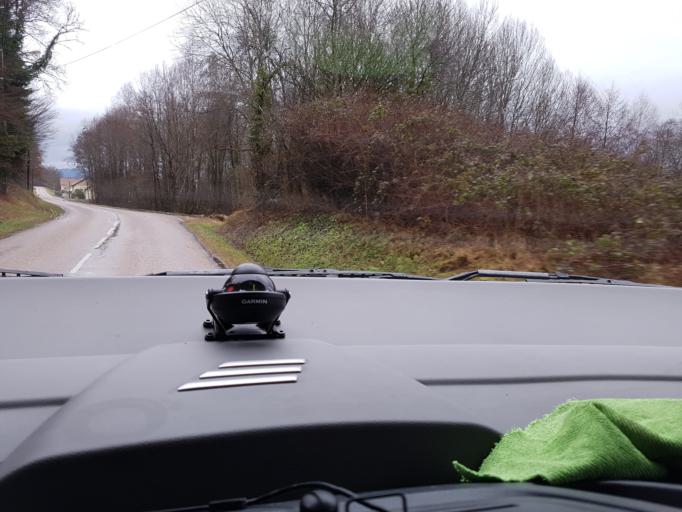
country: FR
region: Lorraine
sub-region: Departement des Vosges
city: Saint-Die-des-Vosges
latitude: 48.2976
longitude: 6.9169
